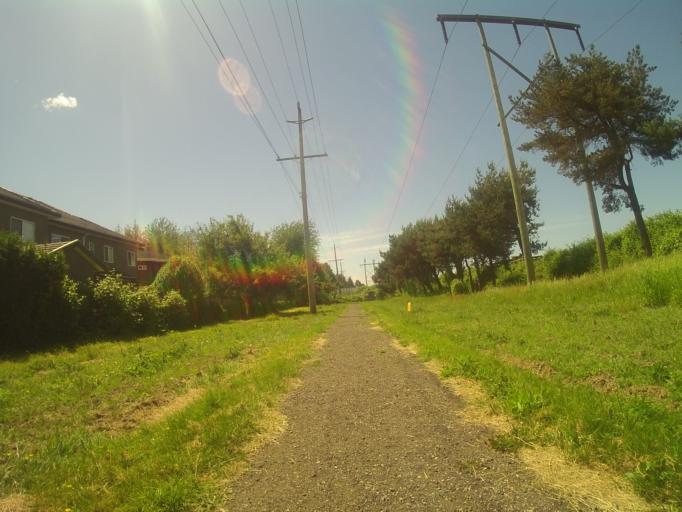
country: CA
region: British Columbia
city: Richmond
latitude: 49.1902
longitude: -123.0883
